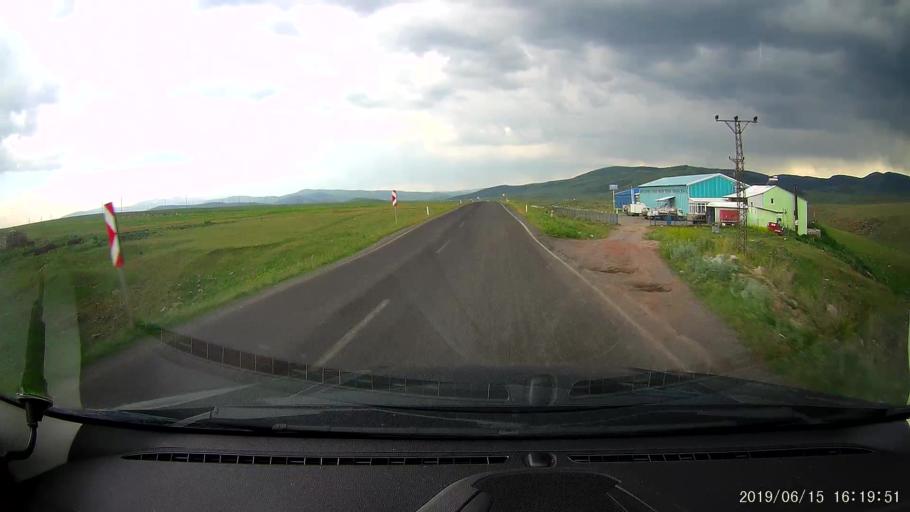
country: TR
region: Ardahan
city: Hanak
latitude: 41.2237
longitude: 42.8498
